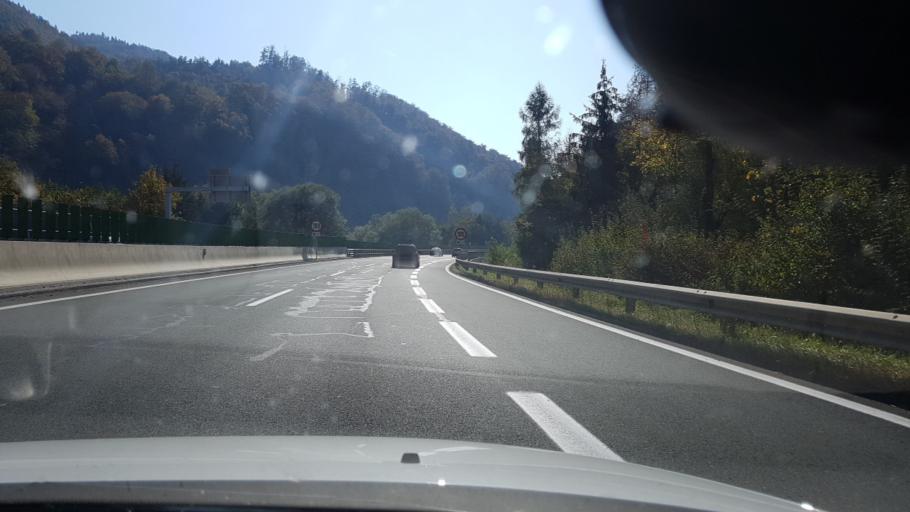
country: AT
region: Styria
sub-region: Politischer Bezirk Graz-Umgebung
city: Peggau
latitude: 47.2275
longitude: 15.3412
